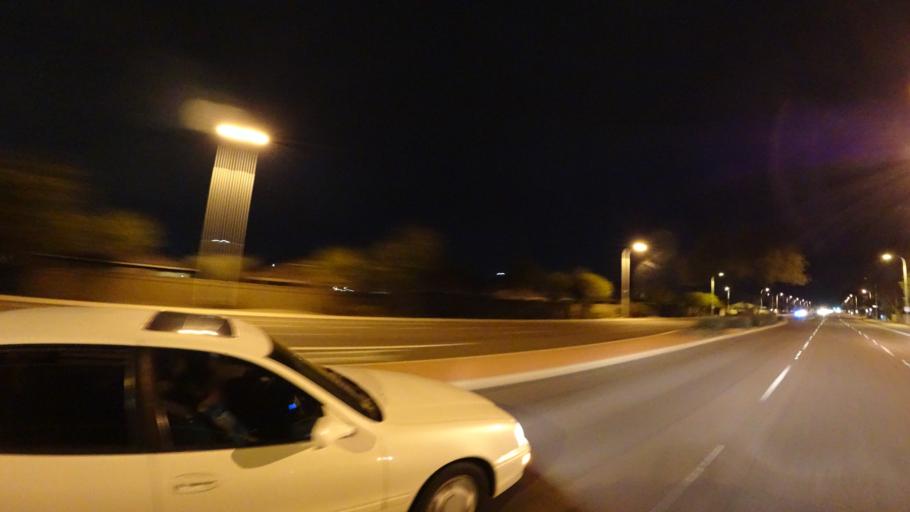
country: US
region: Arizona
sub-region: Maricopa County
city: Chandler
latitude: 33.3062
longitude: -111.8217
